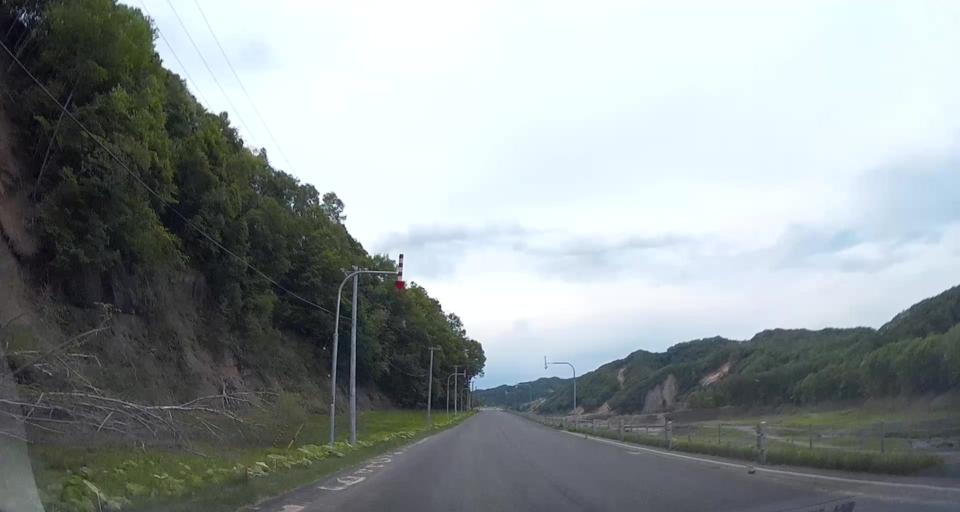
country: JP
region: Hokkaido
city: Chitose
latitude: 42.7869
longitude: 142.0270
